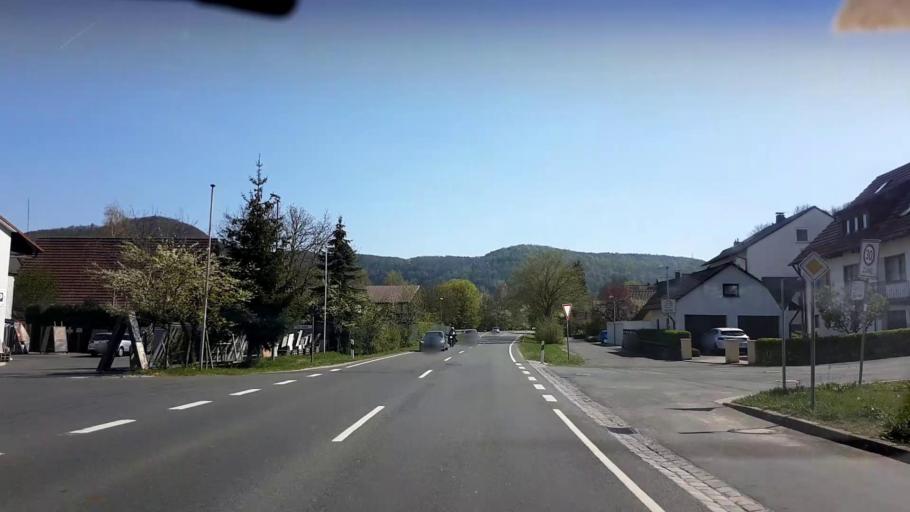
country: DE
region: Bavaria
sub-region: Upper Franconia
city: Ebermannstadt
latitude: 49.7988
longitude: 11.1979
